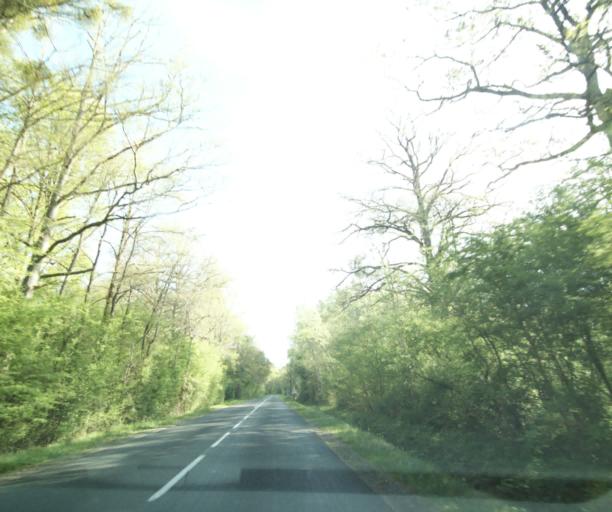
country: FR
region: Ile-de-France
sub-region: Departement de Seine-et-Marne
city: La Chapelle-Gauthier
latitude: 48.4900
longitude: 2.8876
